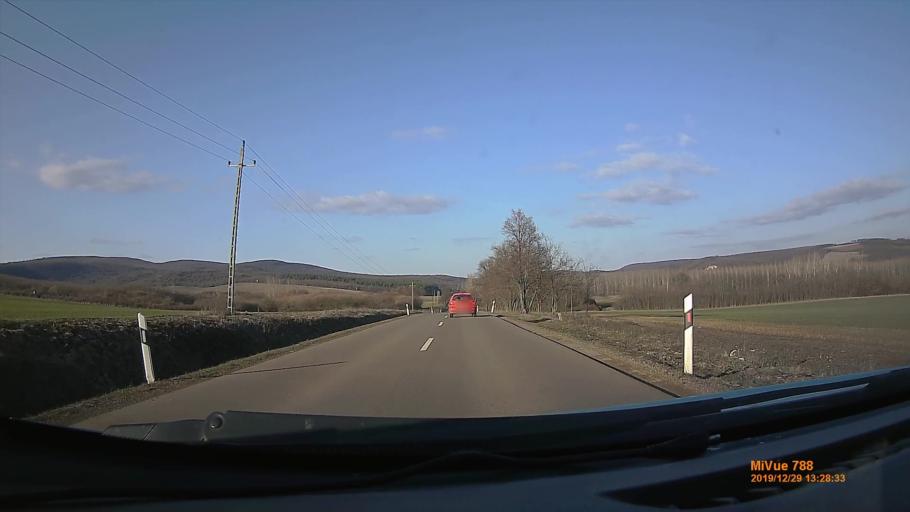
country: HU
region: Heves
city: Verpelet
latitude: 47.8637
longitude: 20.2027
